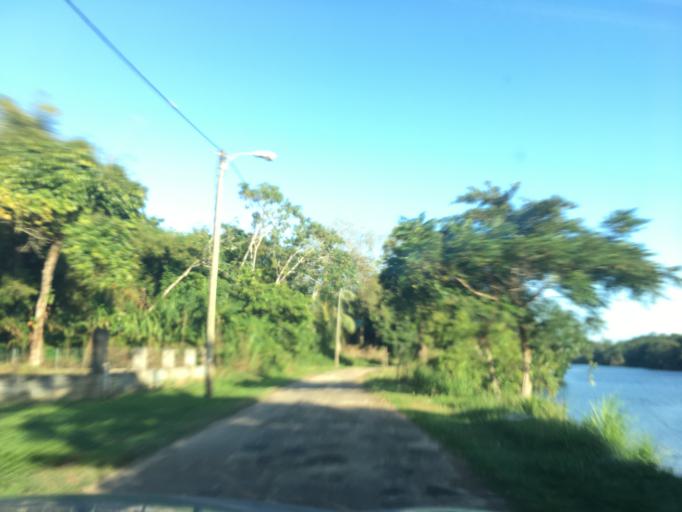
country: BZ
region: Stann Creek
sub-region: Dangriga
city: Dangriga
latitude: 16.8252
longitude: -88.3109
